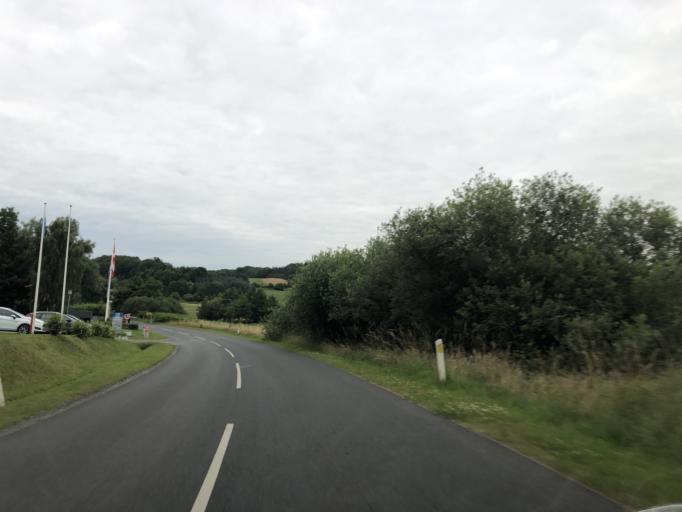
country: DK
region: South Denmark
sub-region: Vejle Kommune
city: Jelling
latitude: 55.7356
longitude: 9.4177
